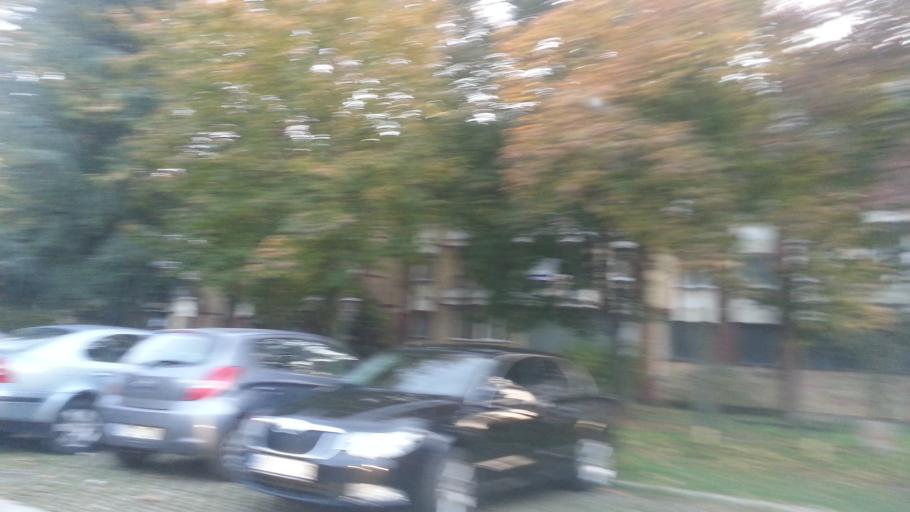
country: RS
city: Novi Banovci
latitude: 44.8954
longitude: 20.2931
